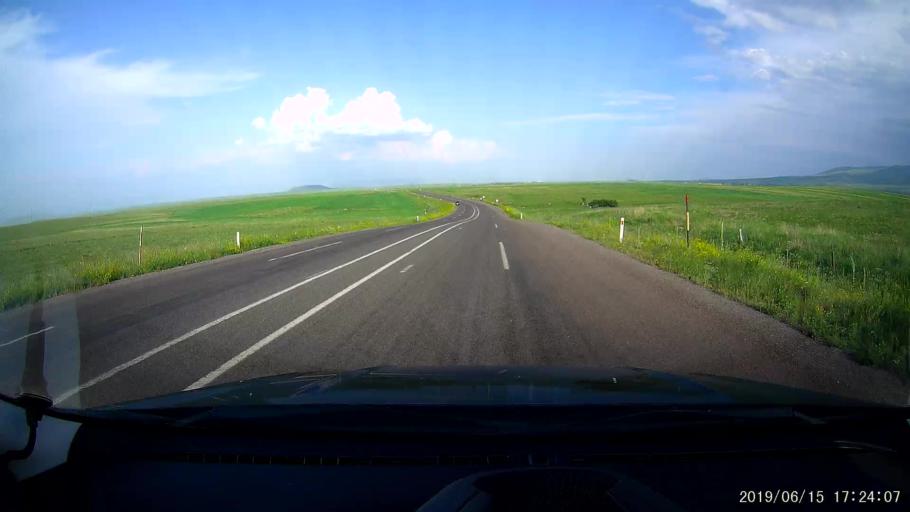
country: TR
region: Kars
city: Basgedikler
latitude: 40.6156
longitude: 43.3767
